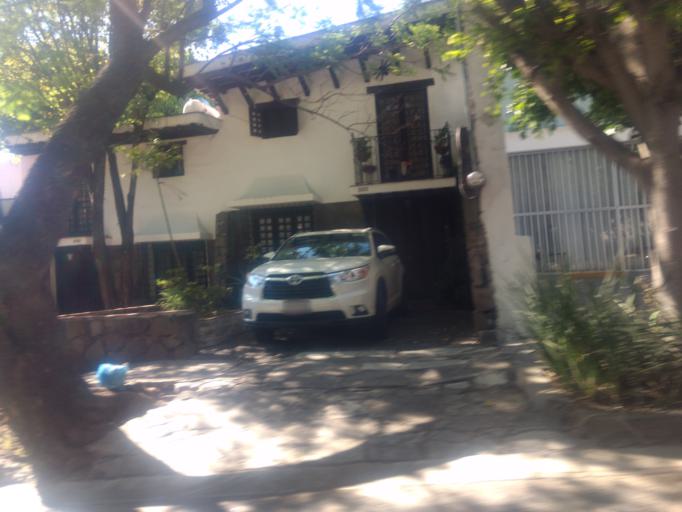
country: MX
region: Jalisco
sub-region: Zapopan
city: Zapopan
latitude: 20.6982
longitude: -103.3784
